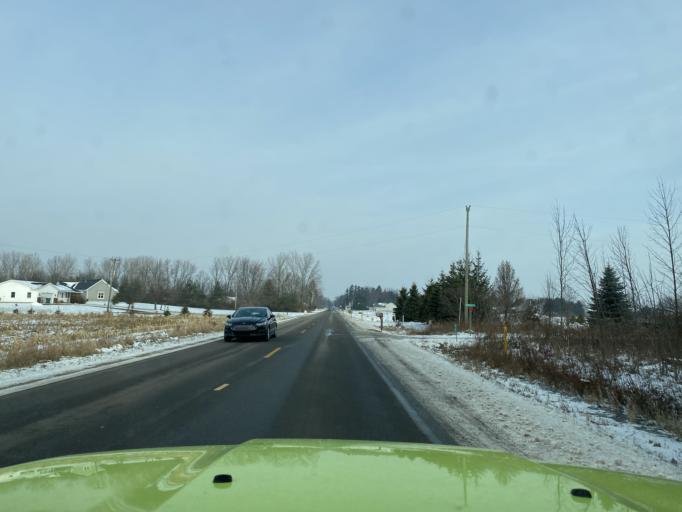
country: US
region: Michigan
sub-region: Ottawa County
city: Allendale
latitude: 42.9643
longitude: -85.9241
